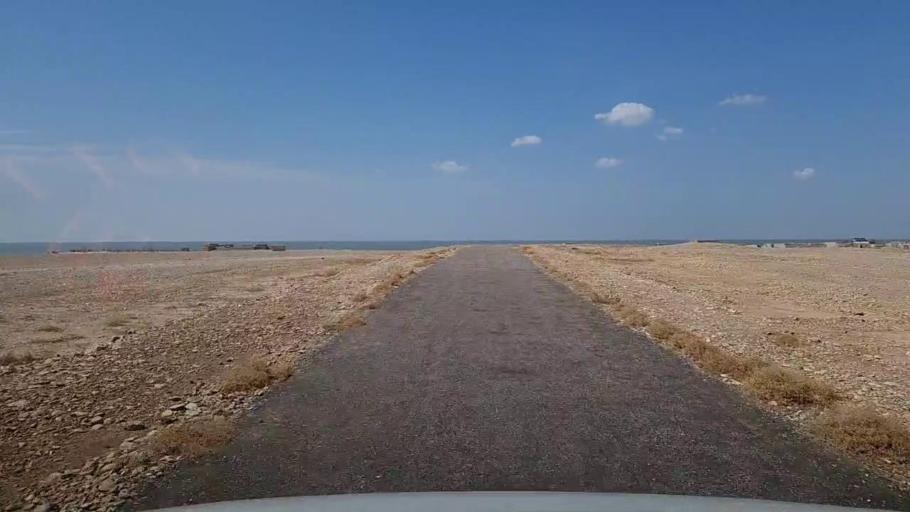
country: PK
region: Sindh
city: Bhan
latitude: 26.3842
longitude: 67.6297
